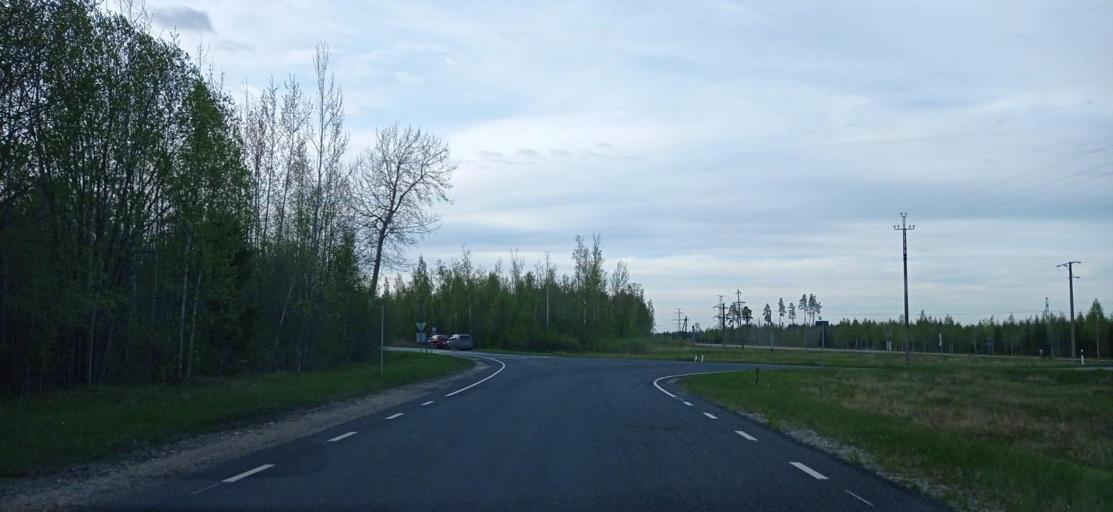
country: EE
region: Paernumaa
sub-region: Tootsi vald
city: Tootsi
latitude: 58.5669
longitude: 24.8095
